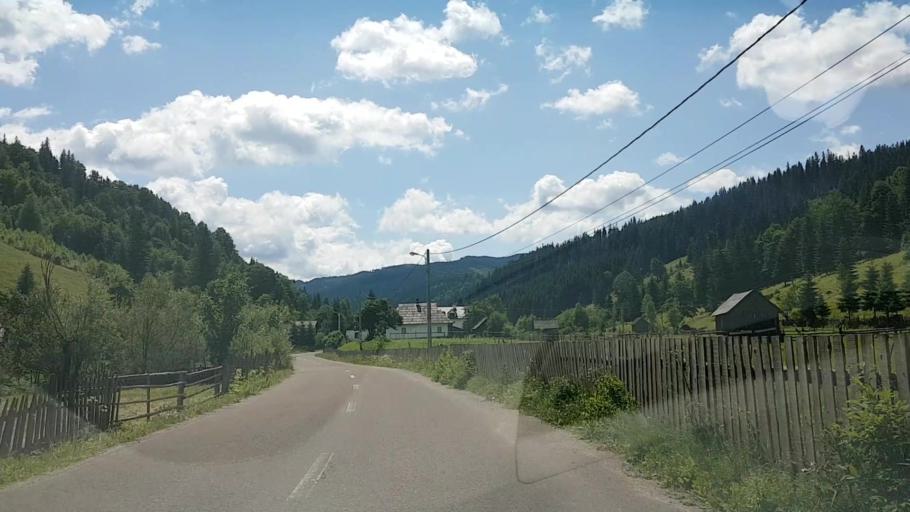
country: RO
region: Suceava
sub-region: Comuna Pojorata
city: Pojorata
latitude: 47.4953
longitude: 25.4824
